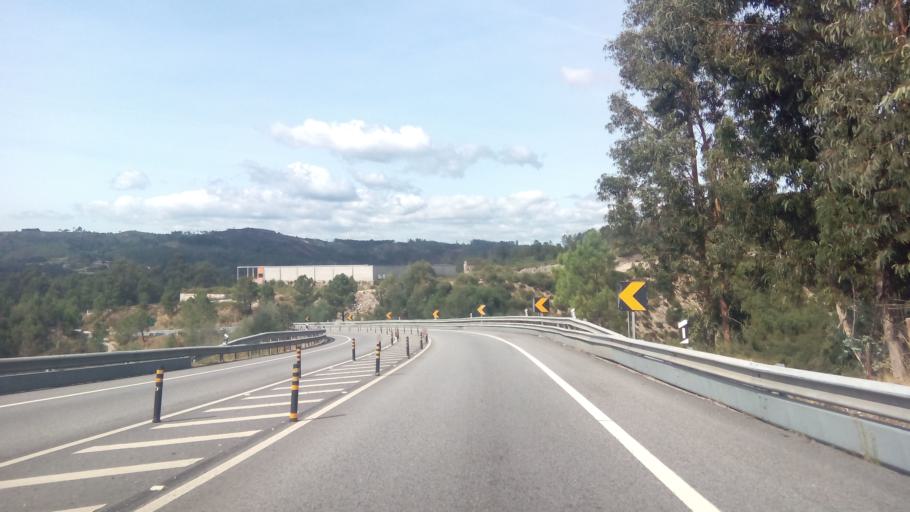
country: PT
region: Porto
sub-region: Amarante
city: Amarante
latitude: 41.2689
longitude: -7.9852
